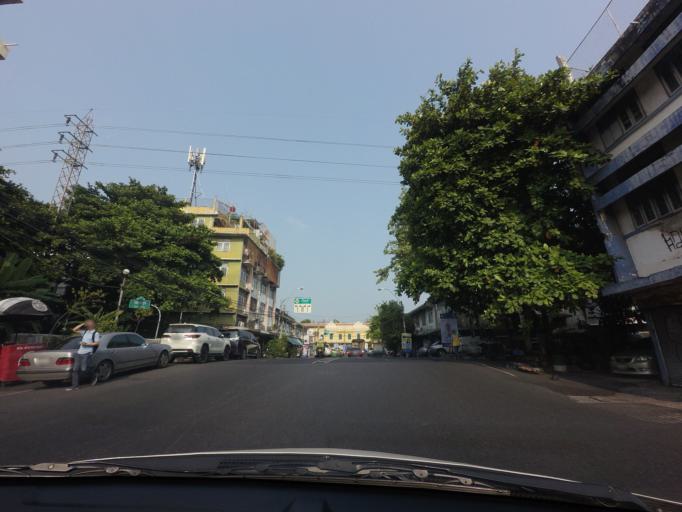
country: TH
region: Bangkok
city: Bangkok
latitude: 13.7489
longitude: 100.5045
